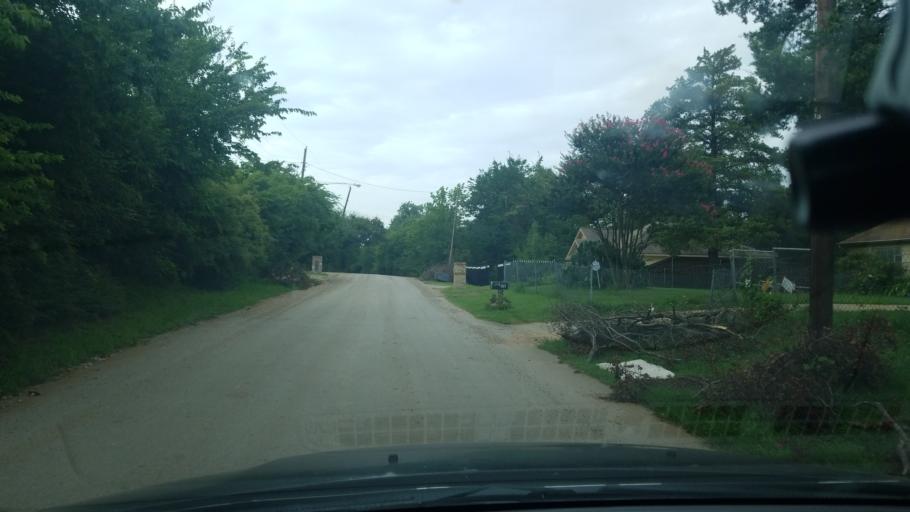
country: US
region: Texas
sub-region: Dallas County
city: Balch Springs
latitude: 32.7320
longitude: -96.6619
